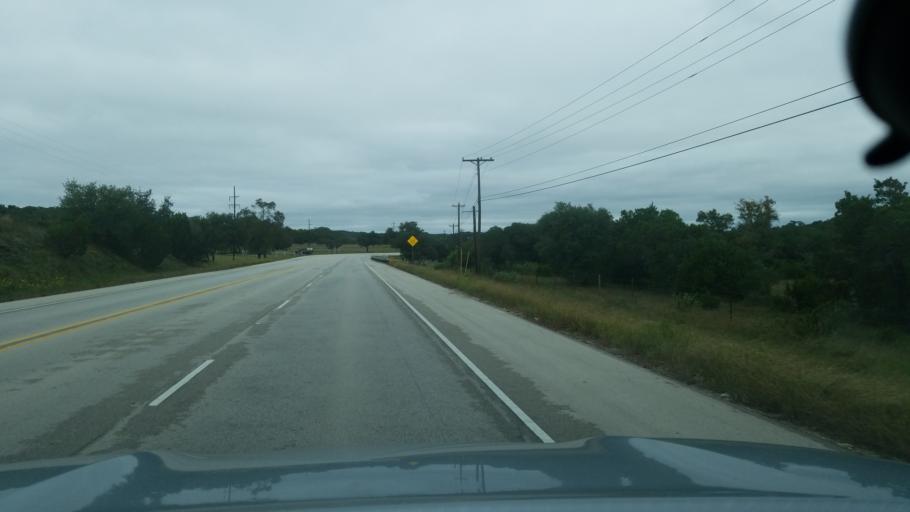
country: US
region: Texas
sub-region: Blanco County
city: Blanco
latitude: 29.9697
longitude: -98.4111
